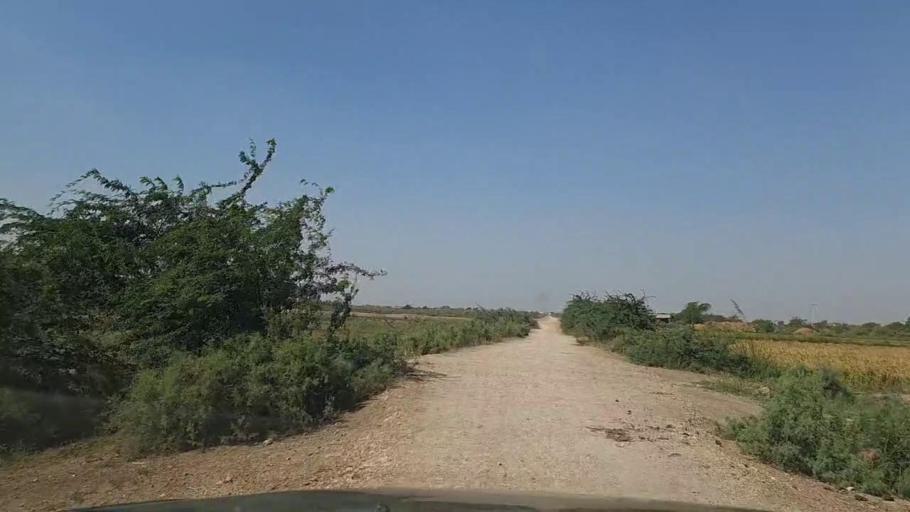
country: PK
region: Sindh
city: Daro Mehar
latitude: 24.8323
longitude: 68.1436
